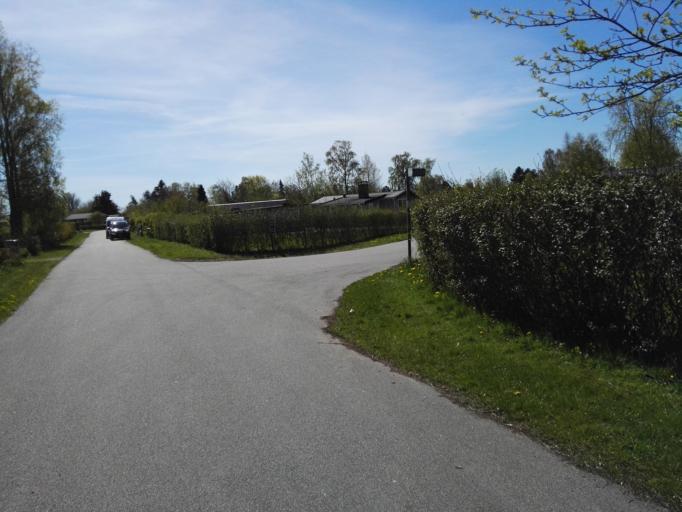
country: DK
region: Capital Region
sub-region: Frederikssund Kommune
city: Frederikssund
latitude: 55.9059
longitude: 12.0596
